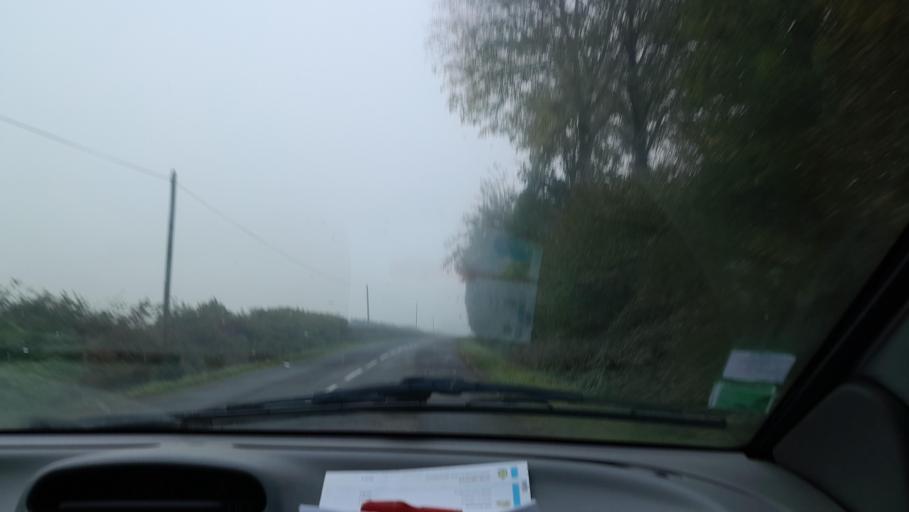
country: FR
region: Brittany
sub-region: Departement d'Ille-et-Vilaine
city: Le Pertre
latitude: 48.0617
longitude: -1.0293
